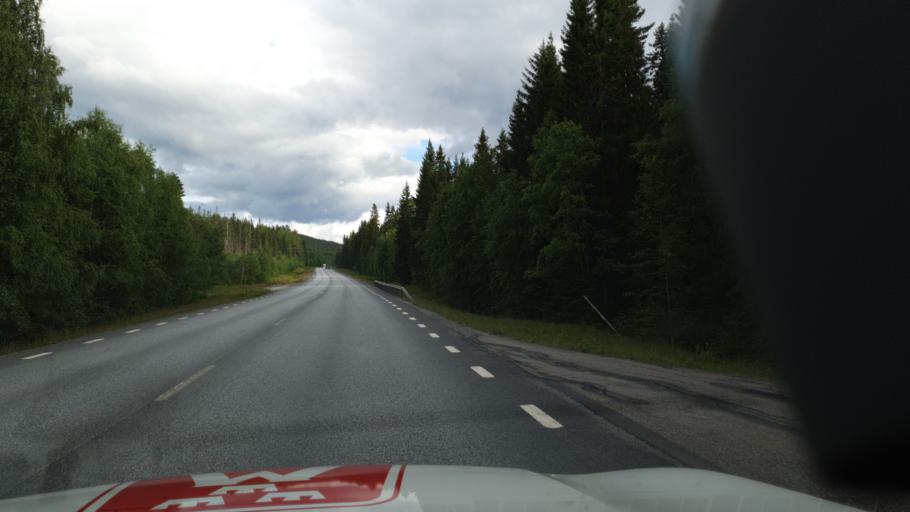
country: SE
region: Vaesterbotten
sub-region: Vannas Kommun
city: Vannasby
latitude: 64.0824
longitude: 19.9798
